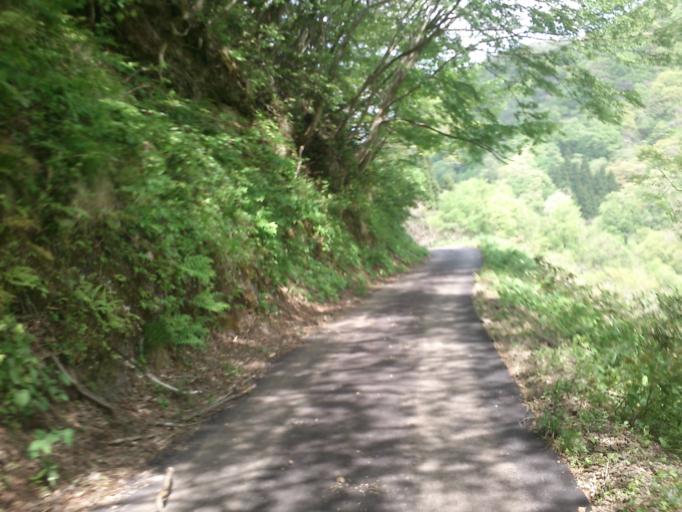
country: JP
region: Kyoto
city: Miyazu
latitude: 35.6450
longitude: 135.1537
